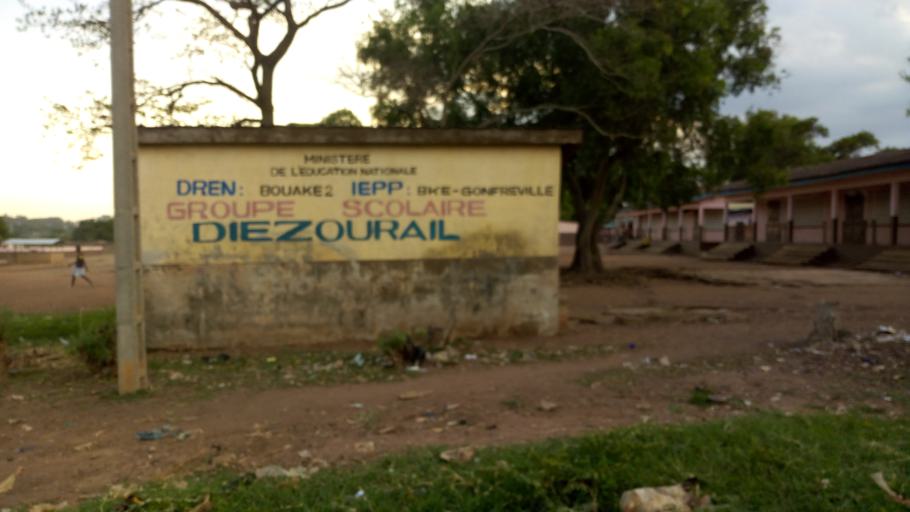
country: CI
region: Vallee du Bandama
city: Bouake
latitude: 7.7003
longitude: -5.0494
